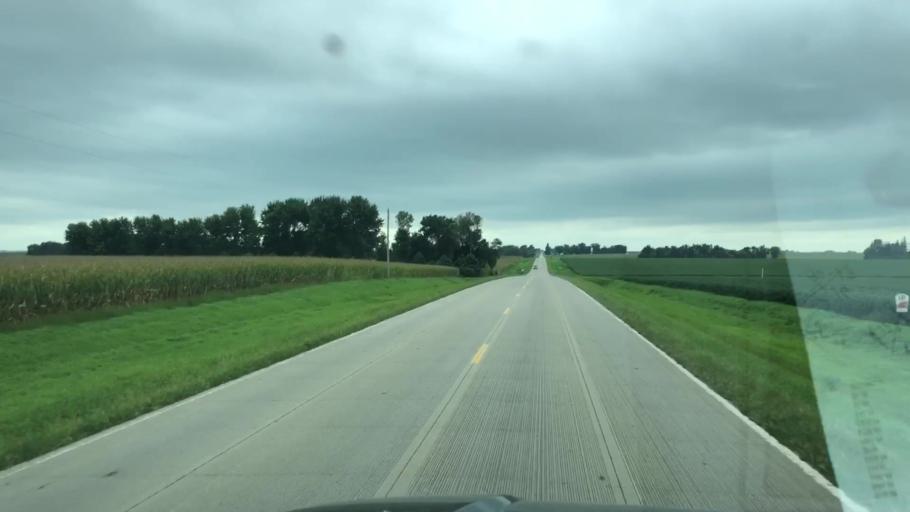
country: US
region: Iowa
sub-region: O'Brien County
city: Sheldon
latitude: 43.1220
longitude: -95.9789
